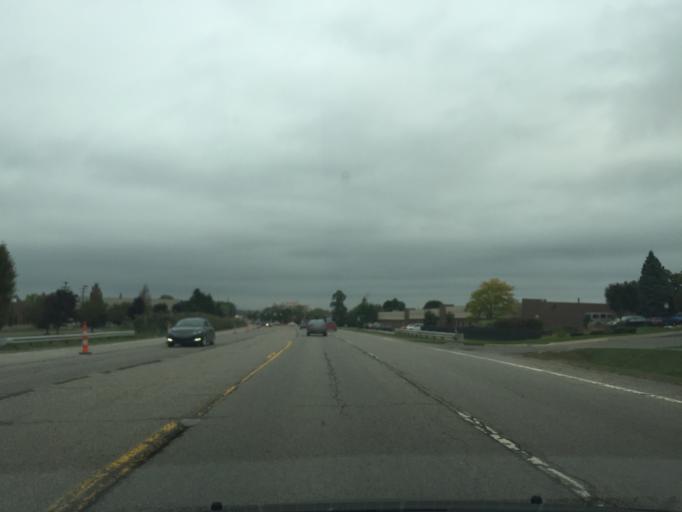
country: US
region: Michigan
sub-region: Oakland County
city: Auburn Hills
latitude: 42.6554
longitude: -83.2459
